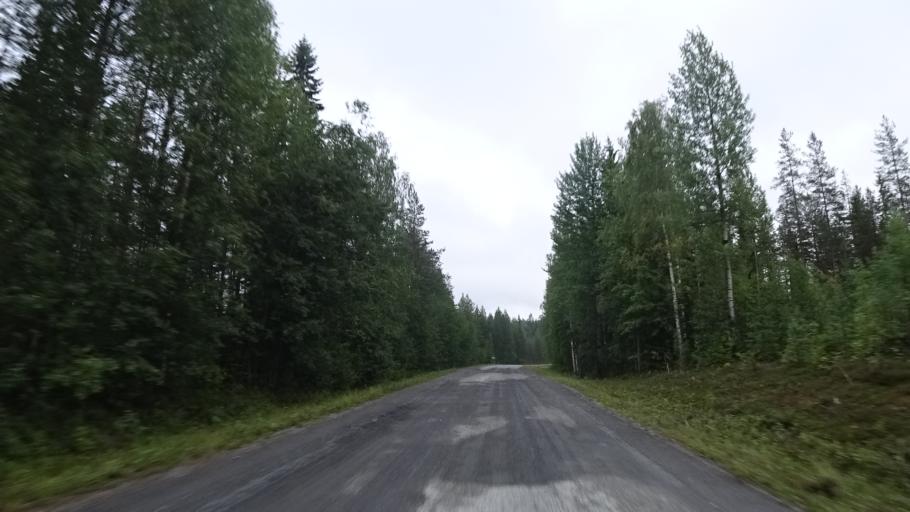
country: FI
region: North Karelia
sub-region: Joensuu
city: Ilomantsi
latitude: 63.2276
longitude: 30.8366
